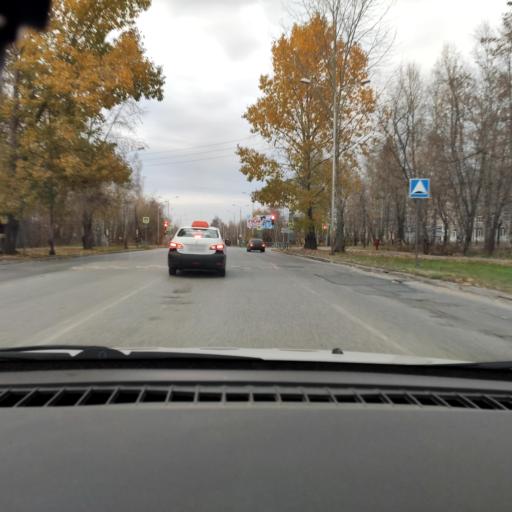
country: RU
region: Perm
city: Perm
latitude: 58.0904
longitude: 56.3821
